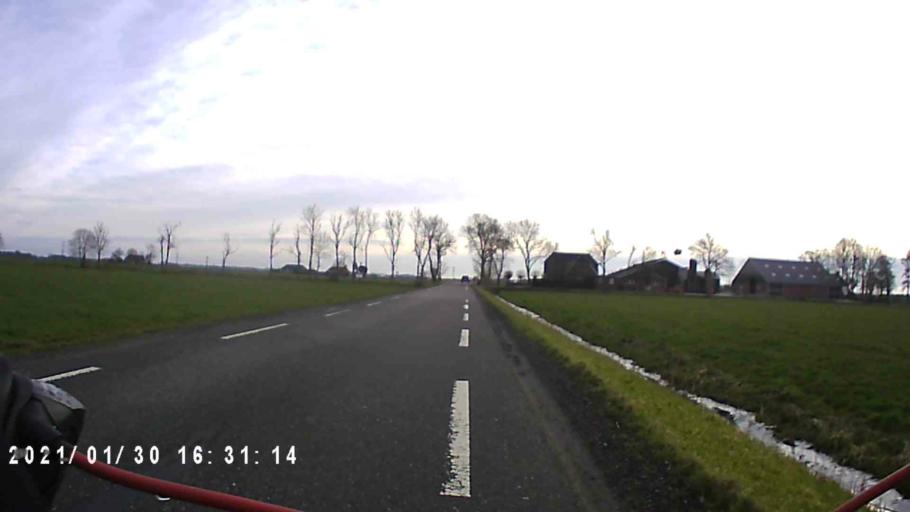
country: NL
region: Groningen
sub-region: Gemeente Zuidhorn
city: Zuidhorn
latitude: 53.2175
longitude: 6.3889
